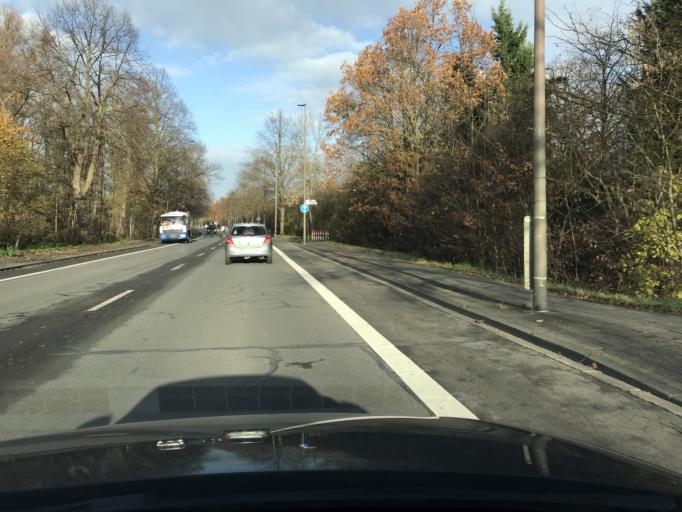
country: DE
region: North Rhine-Westphalia
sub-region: Regierungsbezirk Arnsberg
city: Hamm
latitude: 51.6809
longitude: 7.8521
